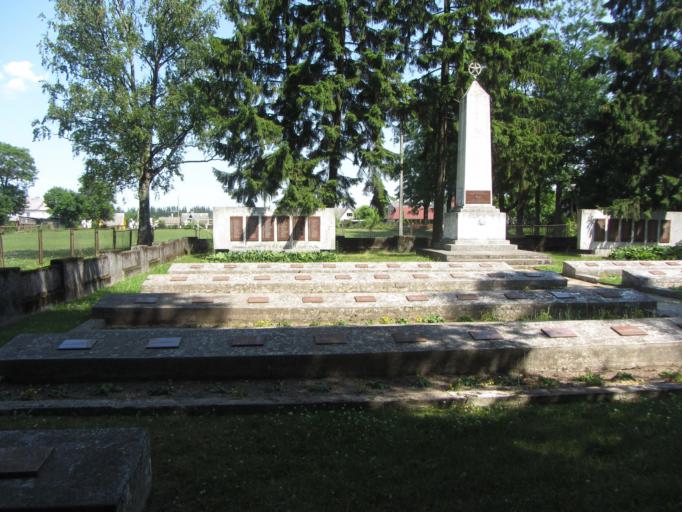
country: LT
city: Sirvintos
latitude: 55.0346
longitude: 24.9721
